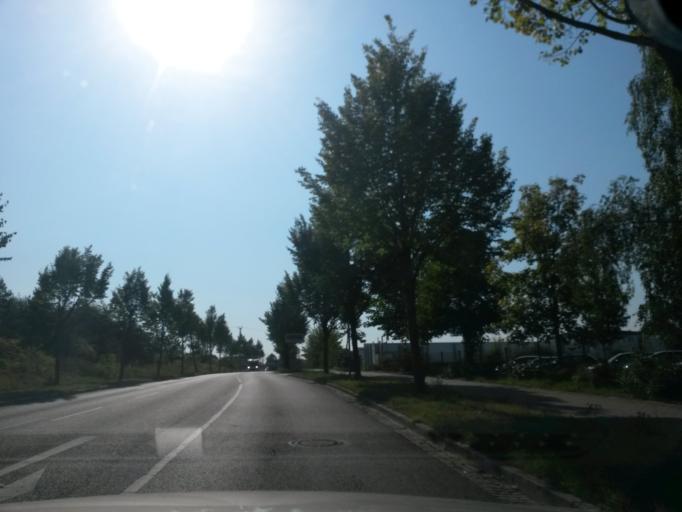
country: DE
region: Brandenburg
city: Angermunde
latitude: 53.0176
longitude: 13.9929
